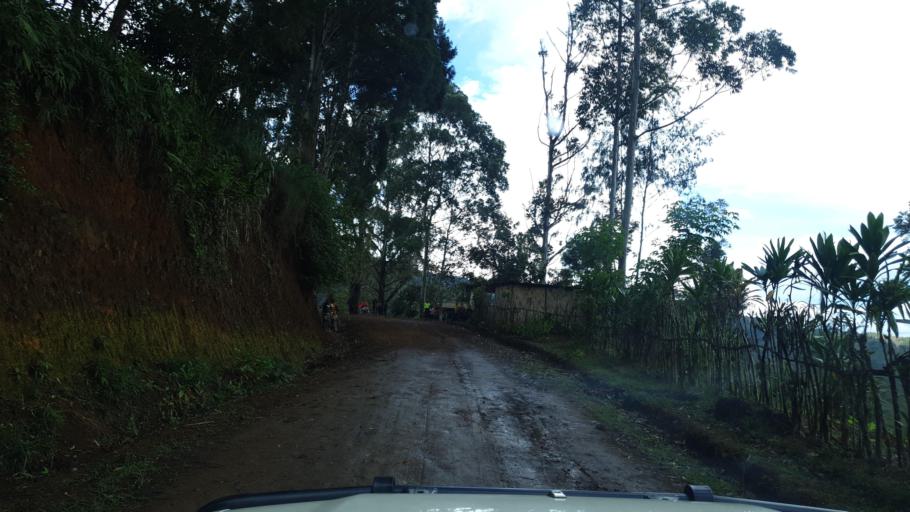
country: PG
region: Eastern Highlands
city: Goroka
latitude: -5.9180
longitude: 145.2569
